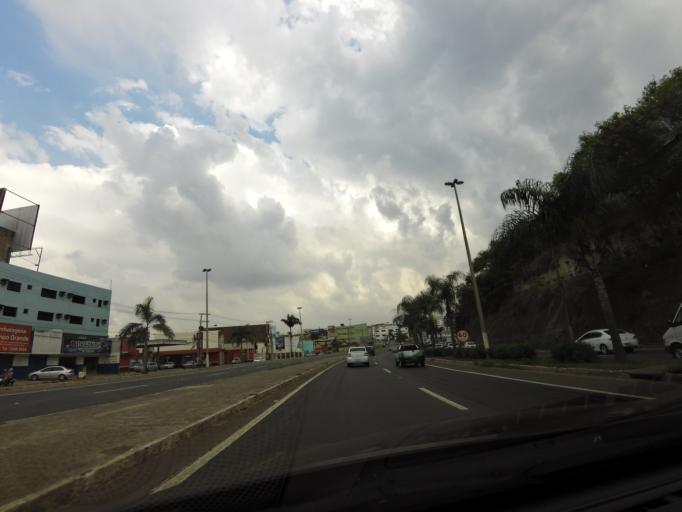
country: BR
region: Espirito Santo
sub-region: Vitoria
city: Vitoria
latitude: -20.3380
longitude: -40.3812
